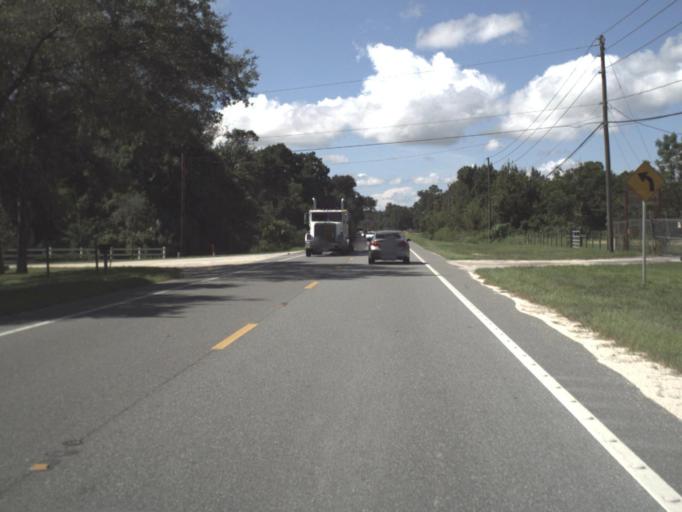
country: US
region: Florida
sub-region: Polk County
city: Davenport
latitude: 28.1834
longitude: -81.5921
